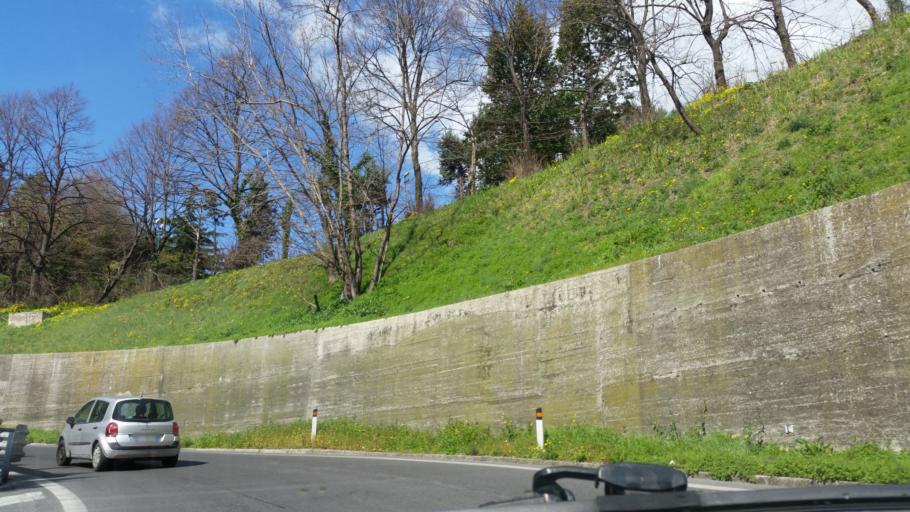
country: IT
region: Campania
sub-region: Provincia di Napoli
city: Napoli
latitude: 40.8675
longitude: 14.2442
